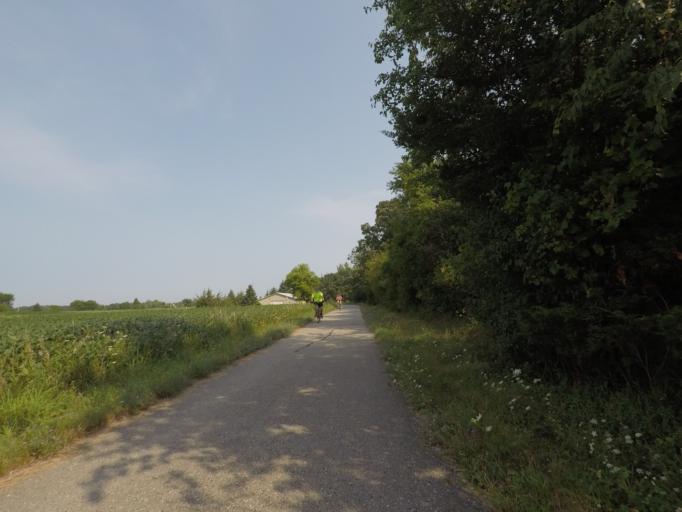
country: US
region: Wisconsin
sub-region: Waukesha County
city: Dousman
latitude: 43.0174
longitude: -88.4470
